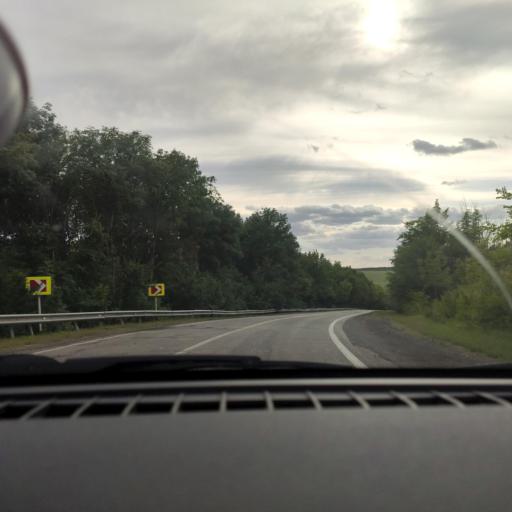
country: RU
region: Samara
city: Krasnyy Yar
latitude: 53.4380
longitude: 50.5860
